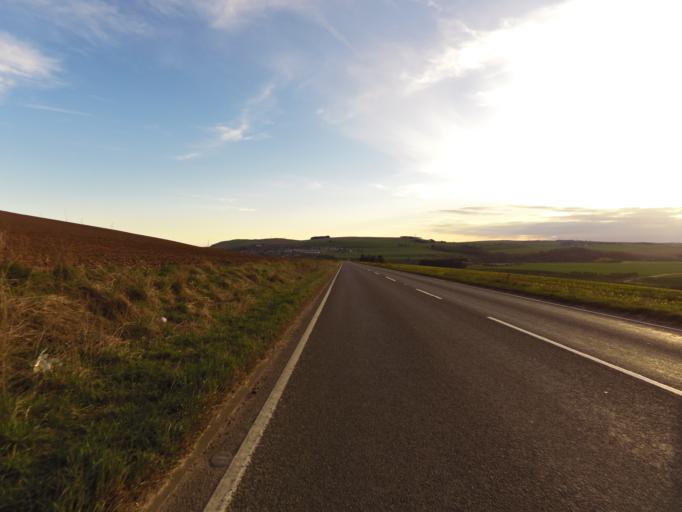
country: GB
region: Scotland
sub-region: Aberdeenshire
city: Inverbervie
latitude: 56.8541
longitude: -2.2723
